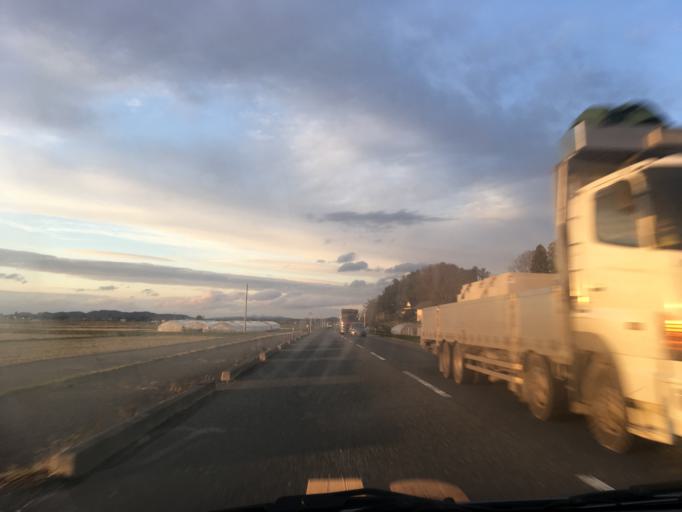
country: JP
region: Miyagi
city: Wakuya
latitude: 38.6928
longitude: 141.2605
